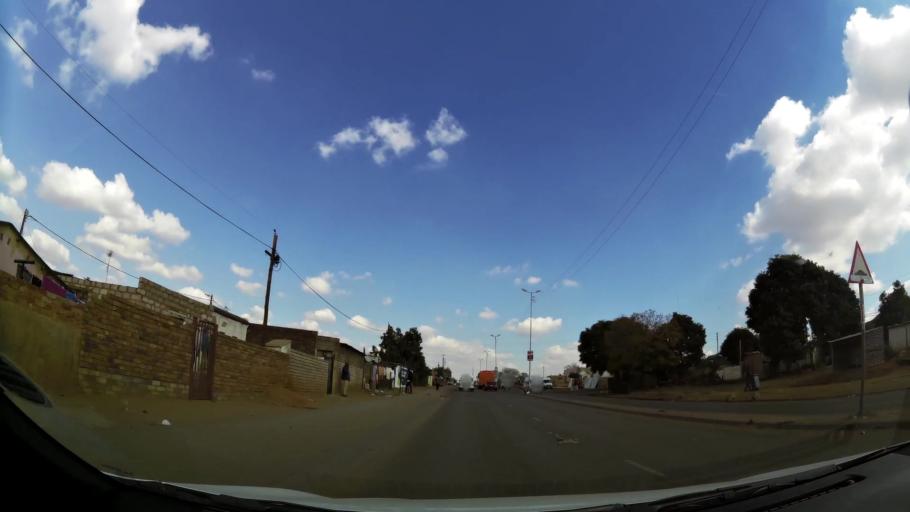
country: ZA
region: Gauteng
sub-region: City of Tshwane Metropolitan Municipality
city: Cullinan
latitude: -25.7019
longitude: 28.3953
